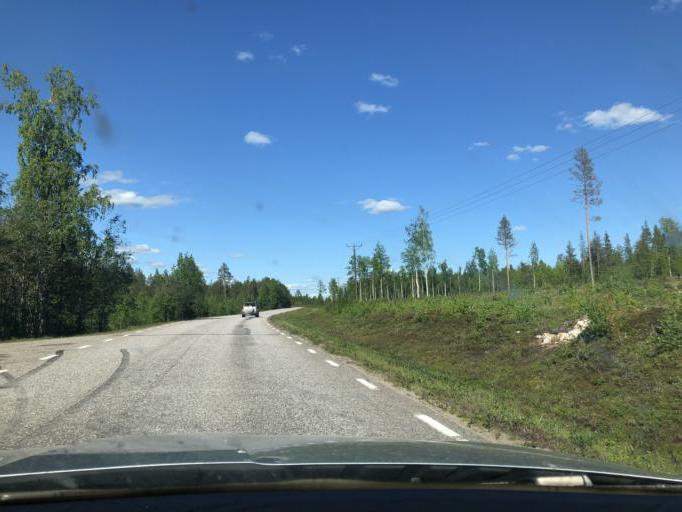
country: SE
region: Norrbotten
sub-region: Kalix Kommun
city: Kalix
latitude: 66.0230
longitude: 23.1566
